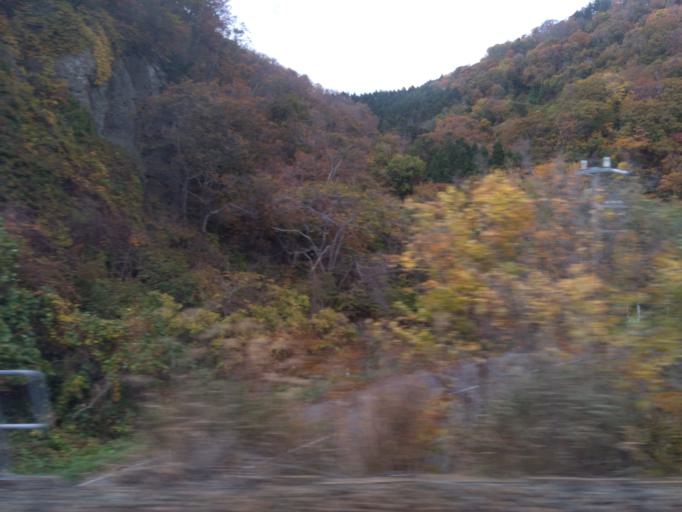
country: JP
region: Hokkaido
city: Niseko Town
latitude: 42.5815
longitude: 140.6237
